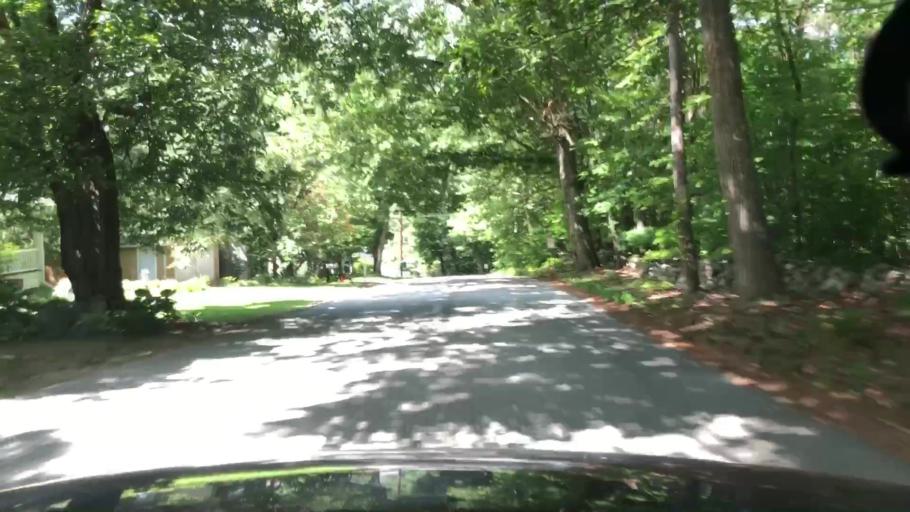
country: US
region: New Hampshire
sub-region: Grafton County
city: Holderness
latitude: 43.7299
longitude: -71.5801
